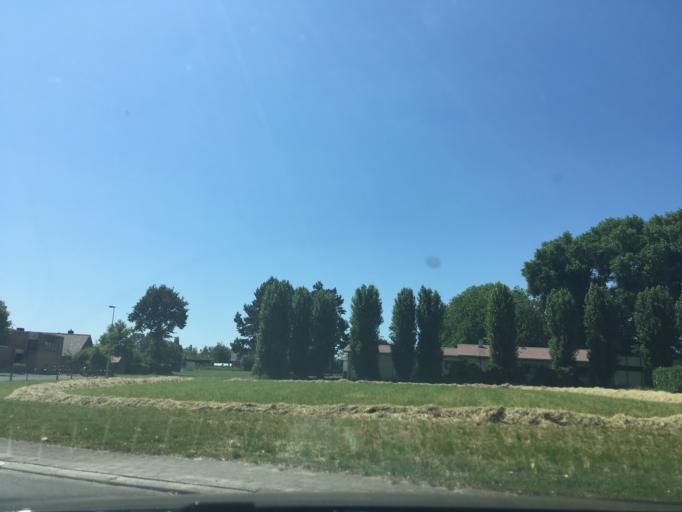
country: BE
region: Flanders
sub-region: Provincie West-Vlaanderen
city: Tielt
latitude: 51.0026
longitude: 3.3136
